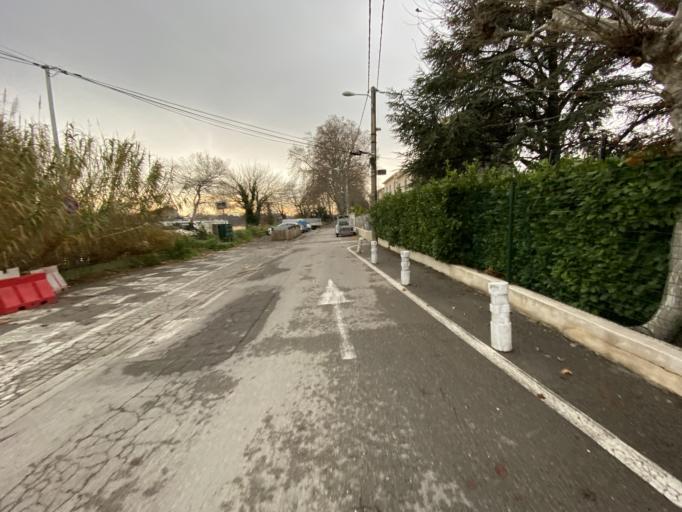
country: FR
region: Provence-Alpes-Cote d'Azur
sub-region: Departement du Vaucluse
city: Avignon
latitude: 43.9503
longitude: 4.7981
